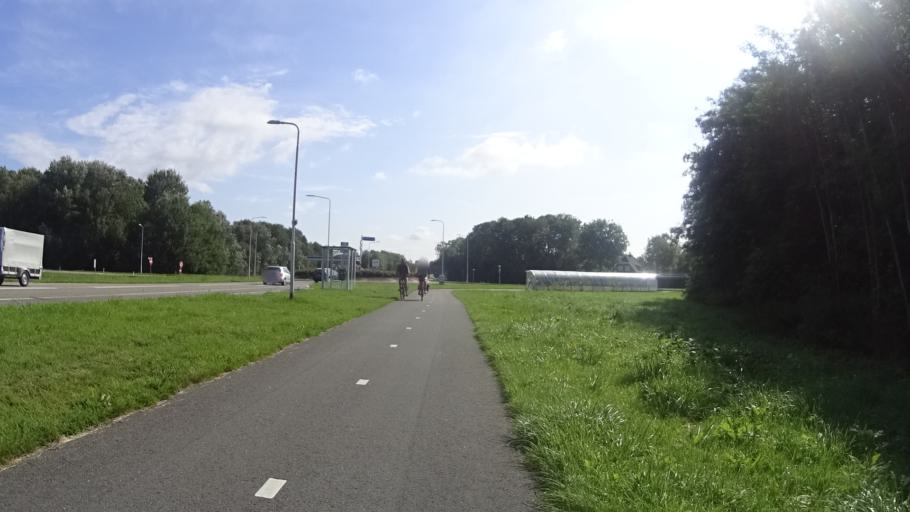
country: NL
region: Friesland
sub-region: Menameradiel
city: Dronryp
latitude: 53.1999
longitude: 5.6475
